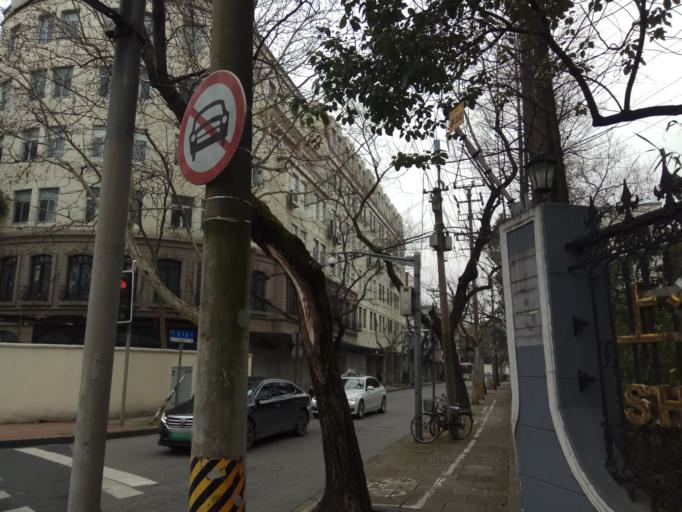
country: CN
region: Shanghai Shi
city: Xuhui
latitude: 31.2106
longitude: 121.4448
